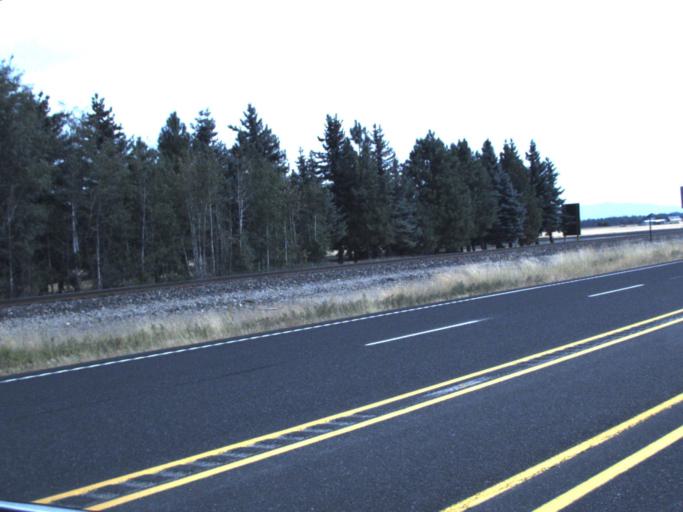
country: US
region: Washington
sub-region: Spokane County
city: Deer Park
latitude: 47.9792
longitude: -117.5246
